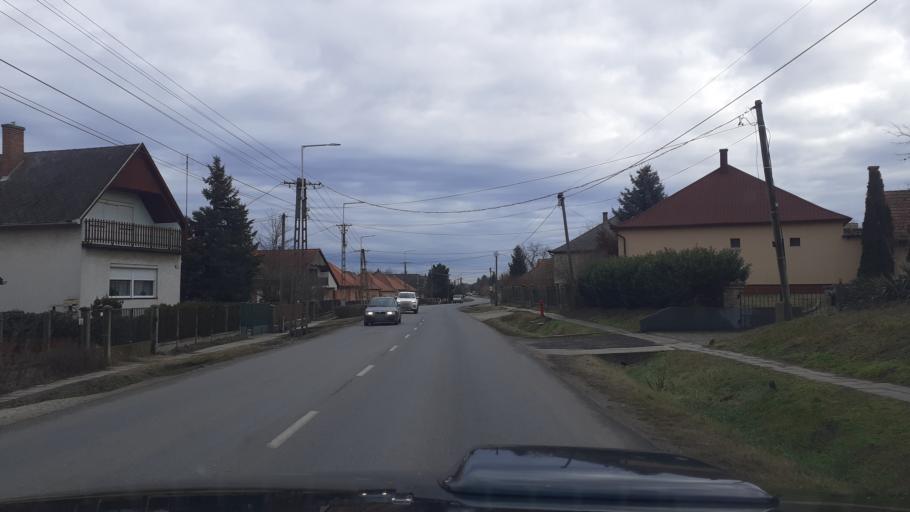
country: HU
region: Fejer
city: Seregelyes
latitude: 47.1133
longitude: 18.5758
